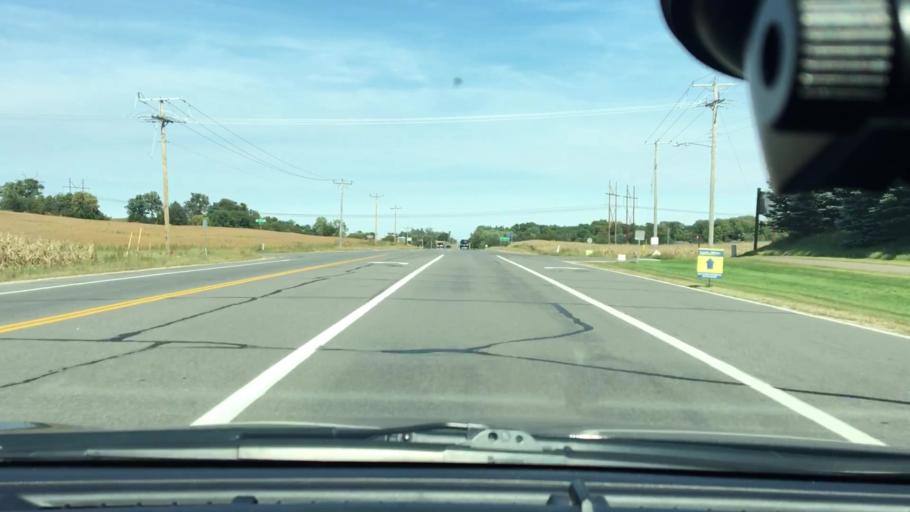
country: US
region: Minnesota
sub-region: Wright County
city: Hanover
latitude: 45.1735
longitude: -93.6656
